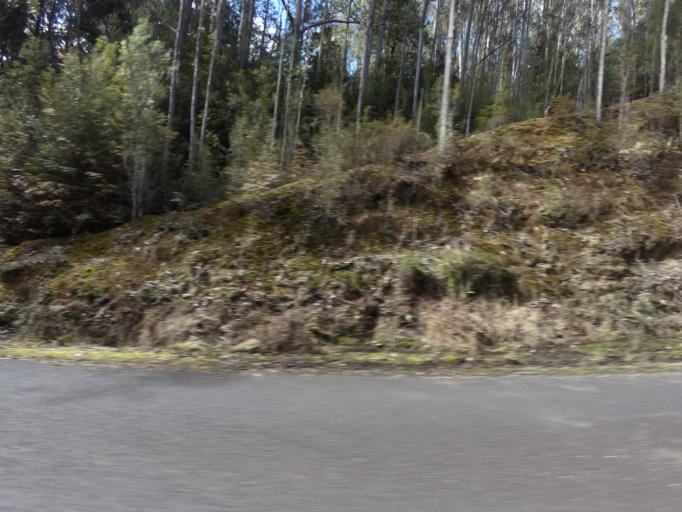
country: AU
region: Tasmania
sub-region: Huon Valley
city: Geeveston
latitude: -42.8238
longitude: 146.3315
